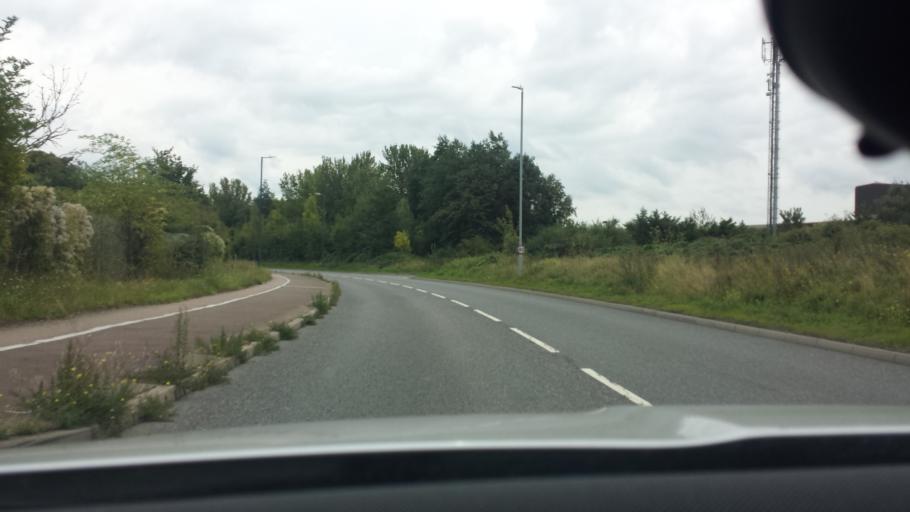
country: GB
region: England
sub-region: Kent
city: Swanscombe
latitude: 51.4383
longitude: 0.3295
